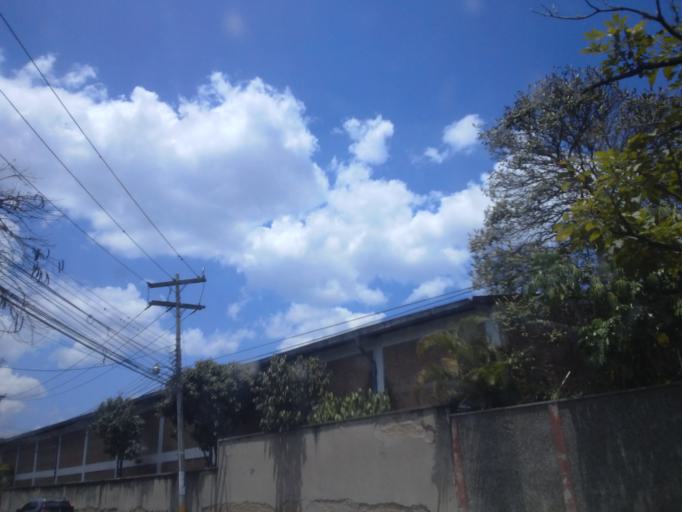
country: HN
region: Francisco Morazan
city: Tegucigalpa
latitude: 14.0579
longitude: -87.2292
